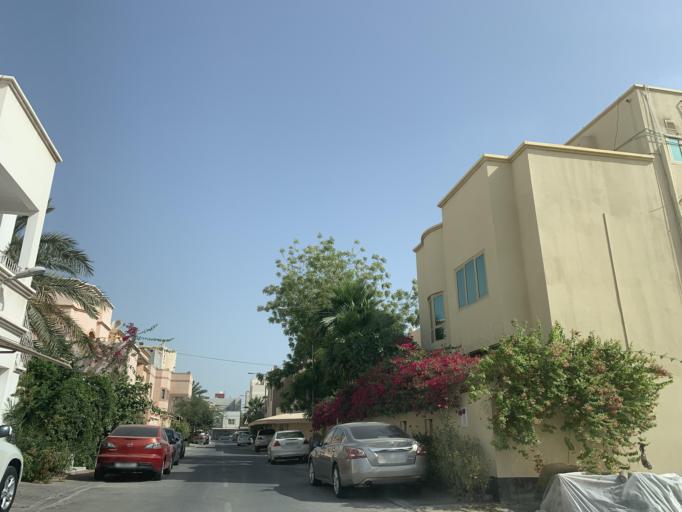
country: BH
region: Northern
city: Ar Rifa'
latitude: 26.1471
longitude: 50.5827
